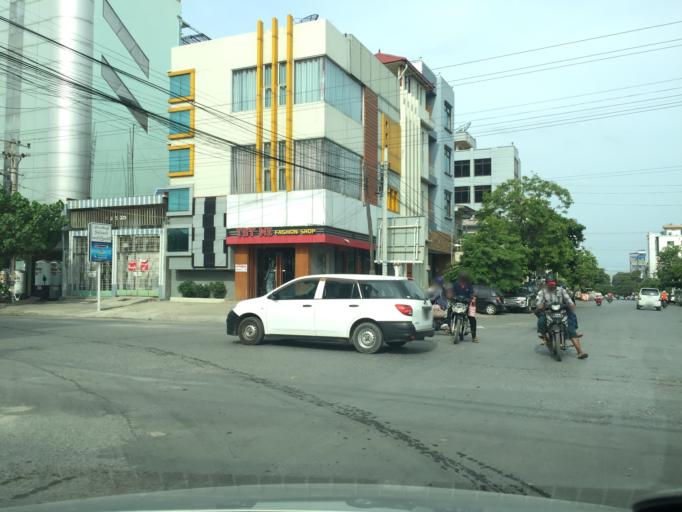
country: MM
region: Mandalay
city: Mandalay
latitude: 21.9742
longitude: 96.0807
